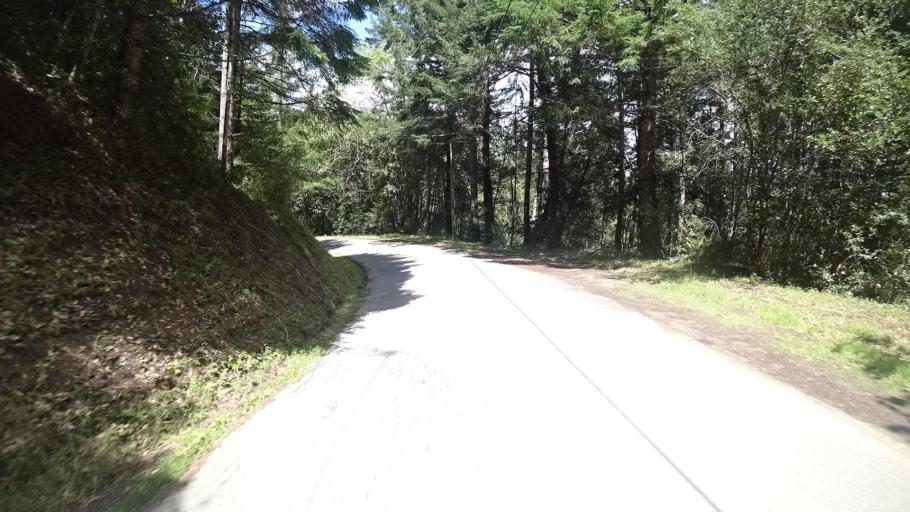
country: US
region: California
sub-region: Humboldt County
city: Blue Lake
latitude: 40.7647
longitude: -123.9468
